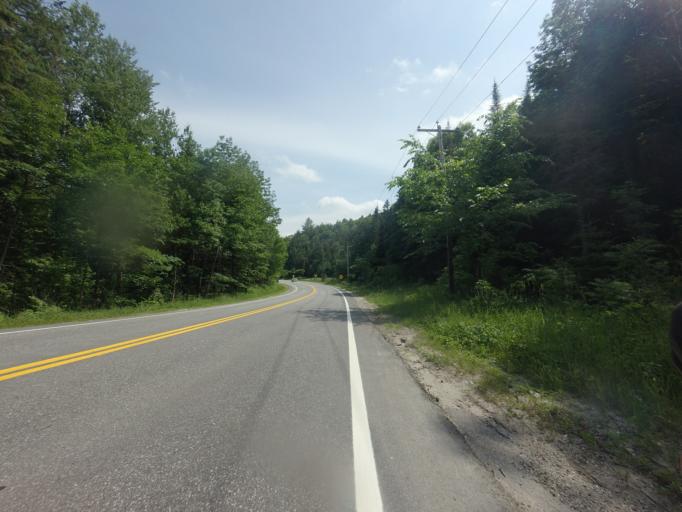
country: CA
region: Quebec
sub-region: Outaouais
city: Wakefield
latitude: 45.7765
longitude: -75.9477
